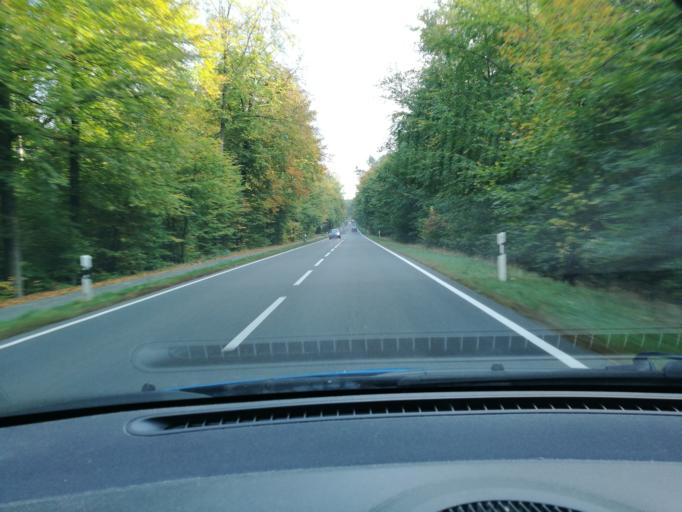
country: DE
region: Lower Saxony
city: Gohrde
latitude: 53.1322
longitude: 10.8962
